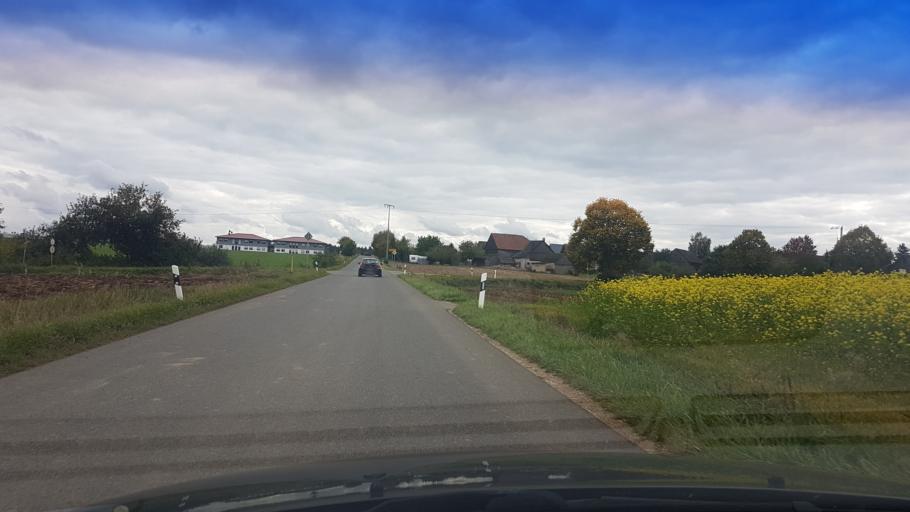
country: DE
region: Bavaria
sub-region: Upper Franconia
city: Wonsees
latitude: 50.0134
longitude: 11.2608
